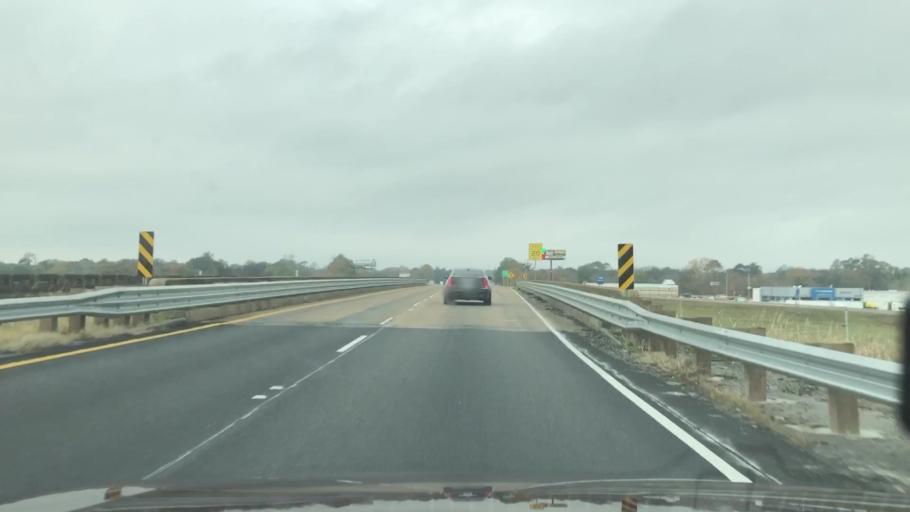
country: US
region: Louisiana
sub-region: Richland Parish
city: Rayville
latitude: 32.4570
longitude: -91.7581
